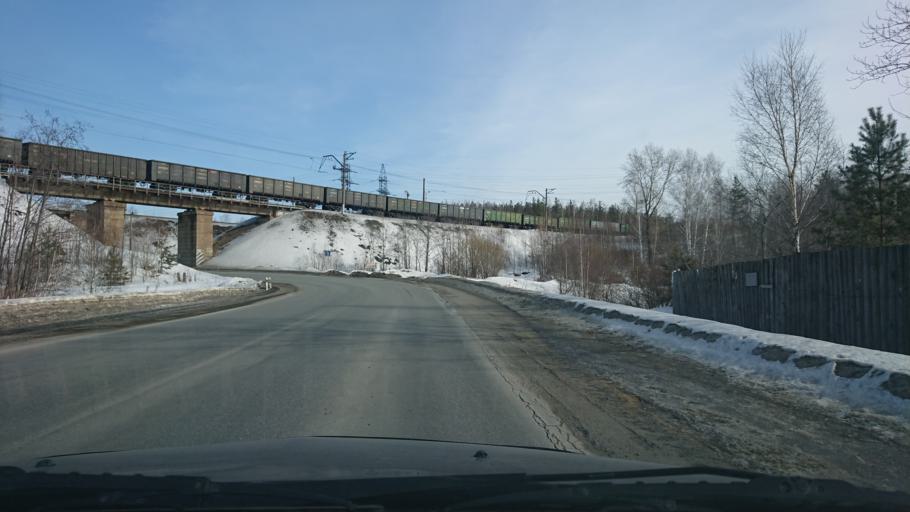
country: RU
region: Sverdlovsk
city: Revda
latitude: 56.8202
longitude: 59.9768
